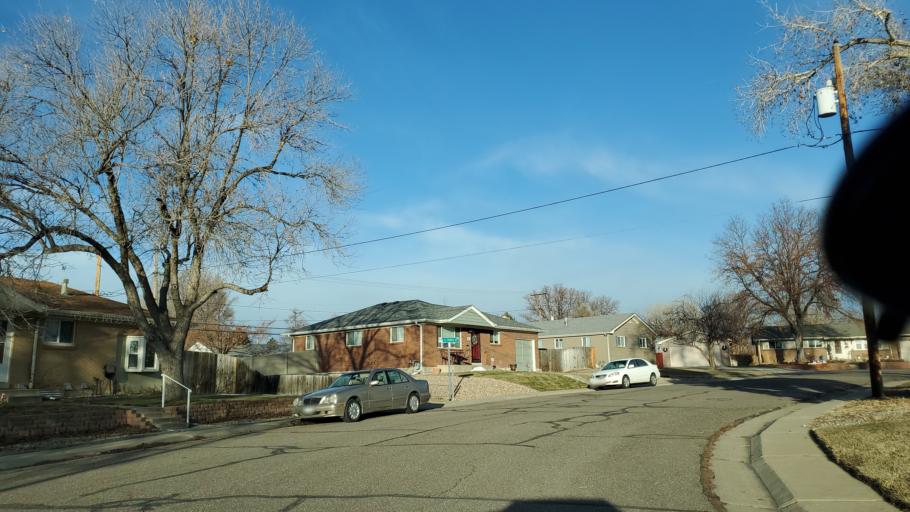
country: US
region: Colorado
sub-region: Adams County
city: Northglenn
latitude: 39.9030
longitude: -104.9633
